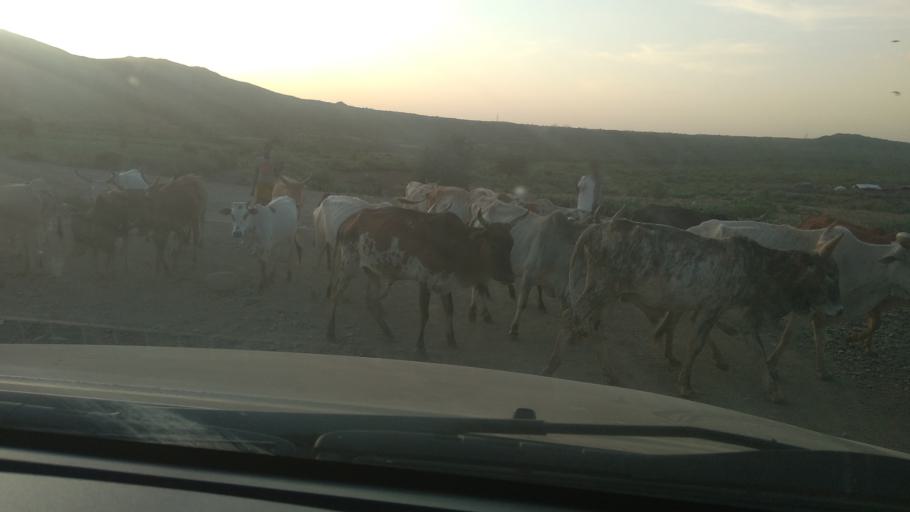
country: ET
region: Oromiya
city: Asbe Teferi
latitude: 9.2504
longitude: 40.7776
